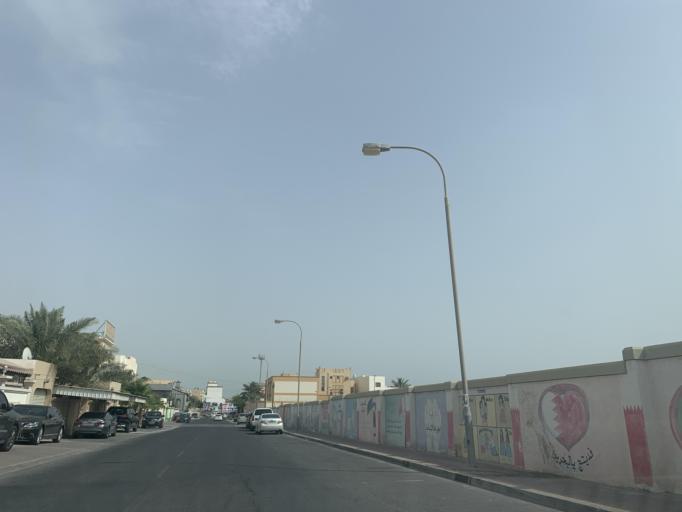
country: BH
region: Northern
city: Ar Rifa'
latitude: 26.1300
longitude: 50.5702
